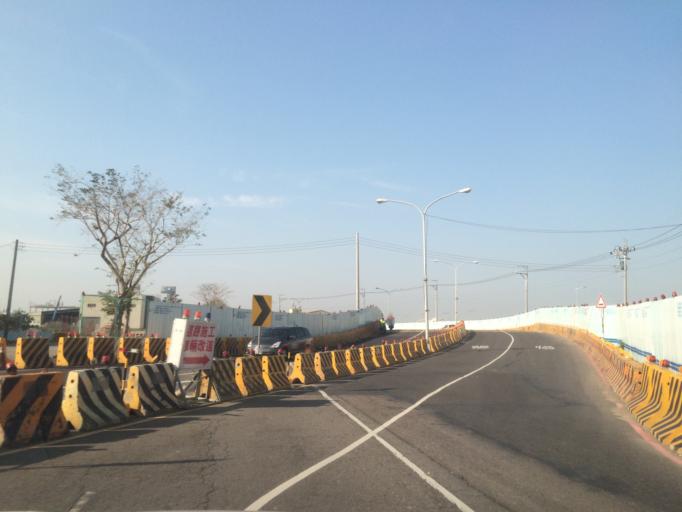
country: TW
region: Taiwan
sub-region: Taichung City
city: Taichung
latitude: 24.1871
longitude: 120.6761
